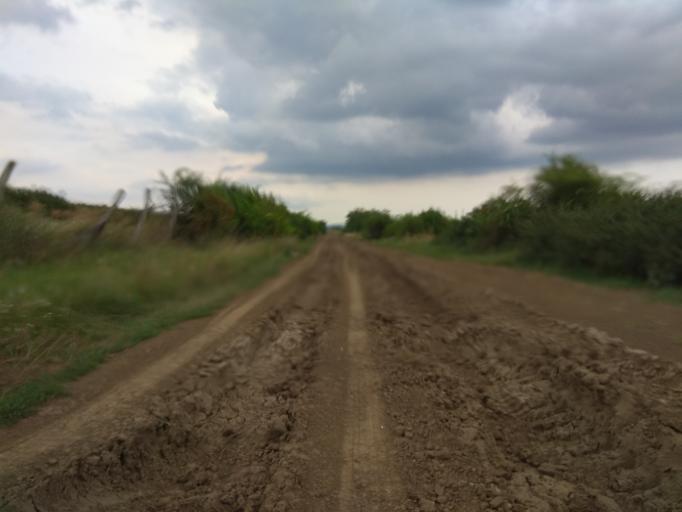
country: HU
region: Borsod-Abauj-Zemplen
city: Megyaszo
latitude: 48.1526
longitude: 21.1081
